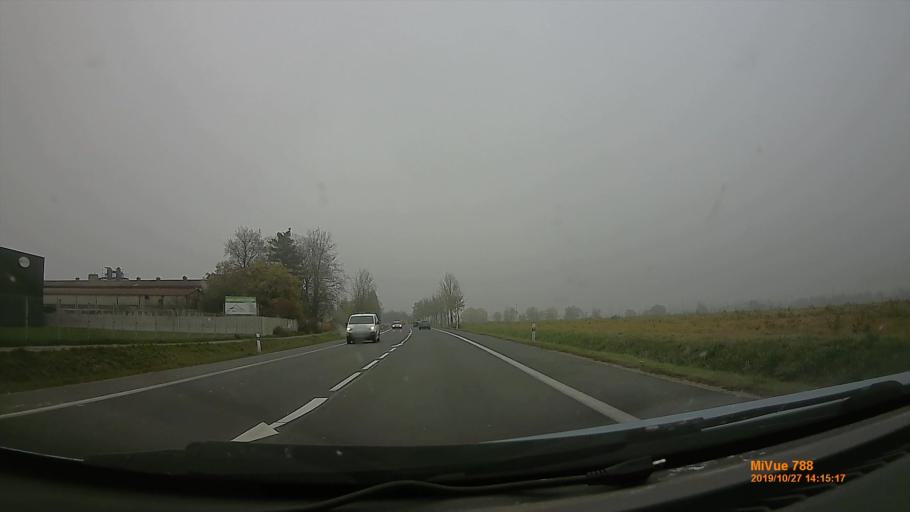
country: CZ
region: Olomoucky
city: Zabreh
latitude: 49.8787
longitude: 16.8923
